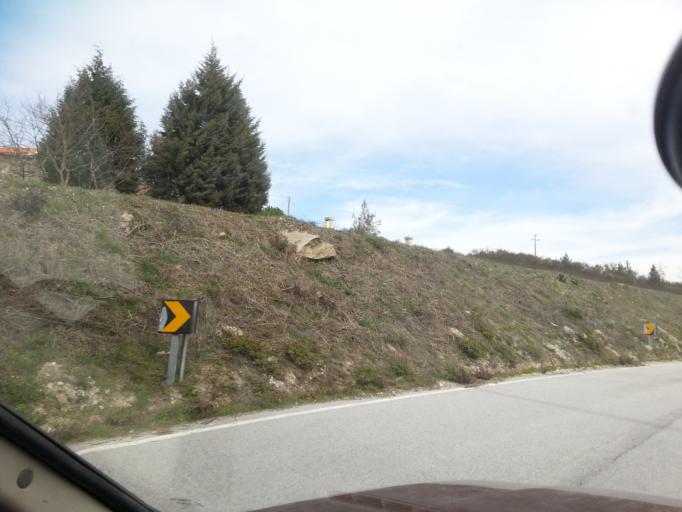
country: PT
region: Guarda
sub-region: Fornos de Algodres
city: Fornos de Algodres
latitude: 40.6083
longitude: -7.5439
